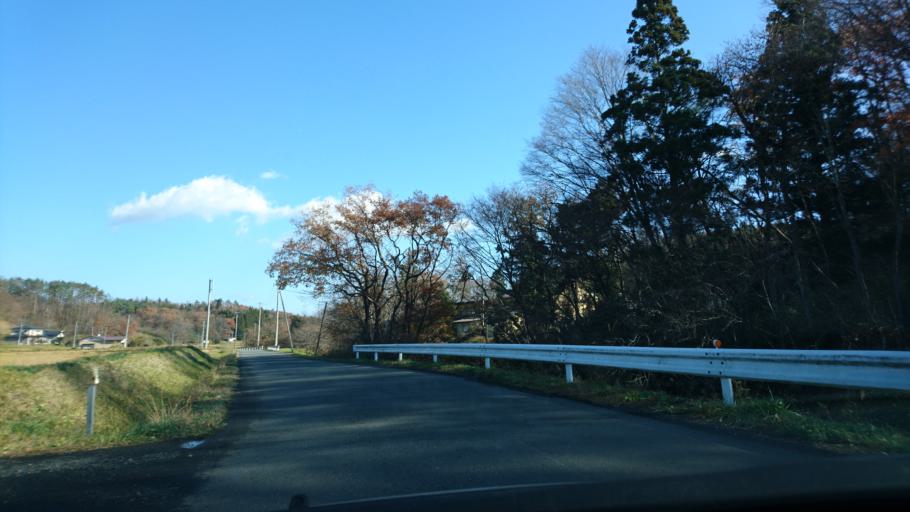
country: JP
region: Iwate
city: Ichinoseki
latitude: 38.9920
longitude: 141.0495
